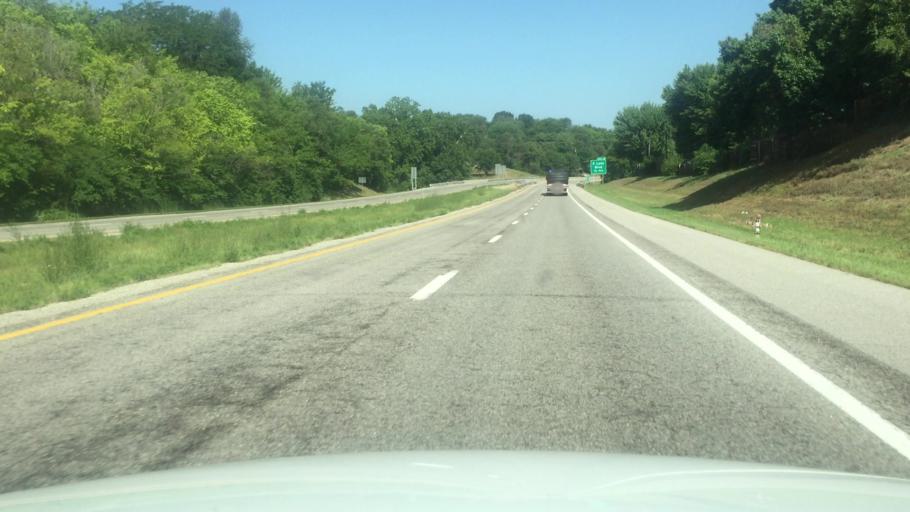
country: US
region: Missouri
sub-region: Buchanan County
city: Saint Joseph
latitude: 39.7260
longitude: -94.8410
